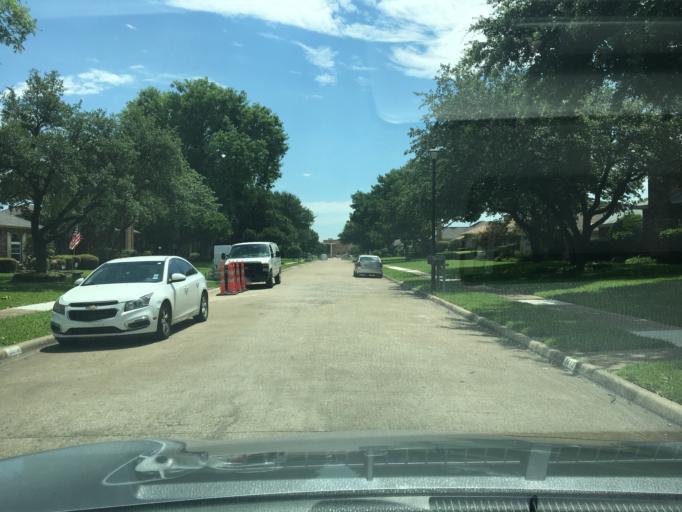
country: US
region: Texas
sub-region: Dallas County
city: Richardson
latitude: 32.9380
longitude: -96.6977
